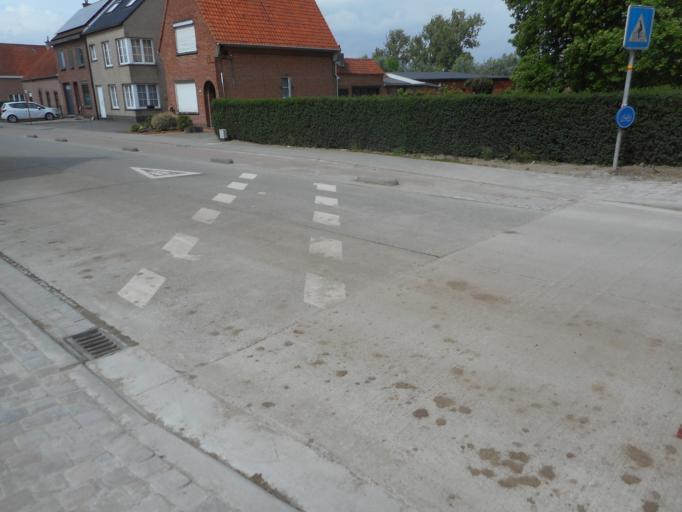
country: BE
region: Flanders
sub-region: Provincie Oost-Vlaanderen
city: Stekene
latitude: 51.1744
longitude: 4.0700
